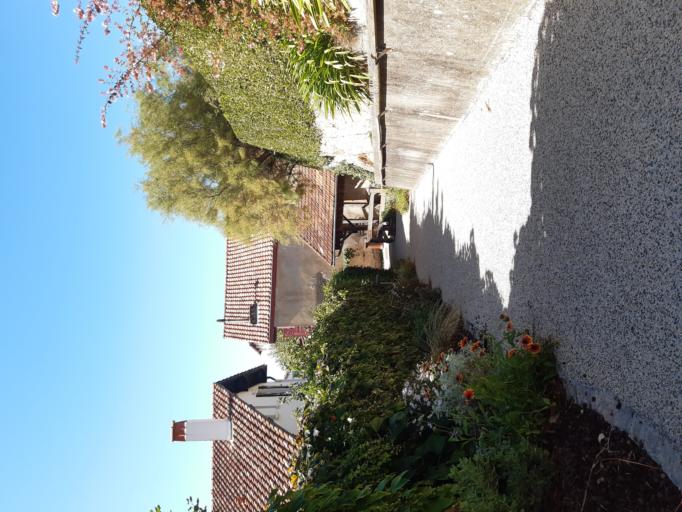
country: FR
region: Aquitaine
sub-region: Departement des Pyrenees-Atlantiques
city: Bidart
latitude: 43.4390
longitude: -1.5903
